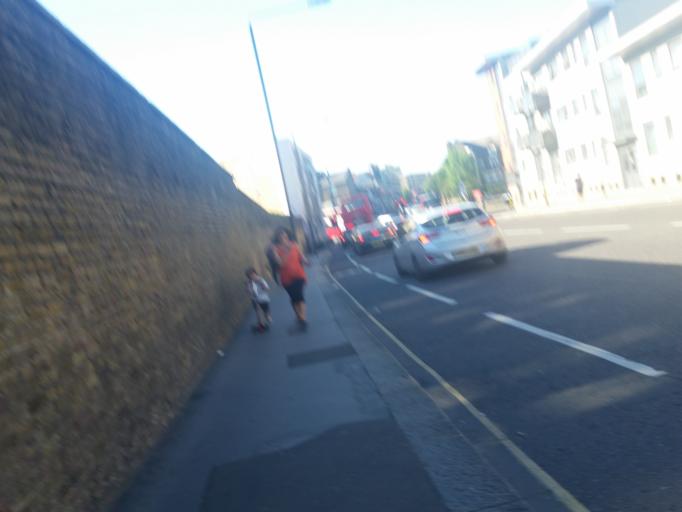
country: GB
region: England
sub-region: Greater London
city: Bayswater
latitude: 51.5271
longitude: -0.2157
